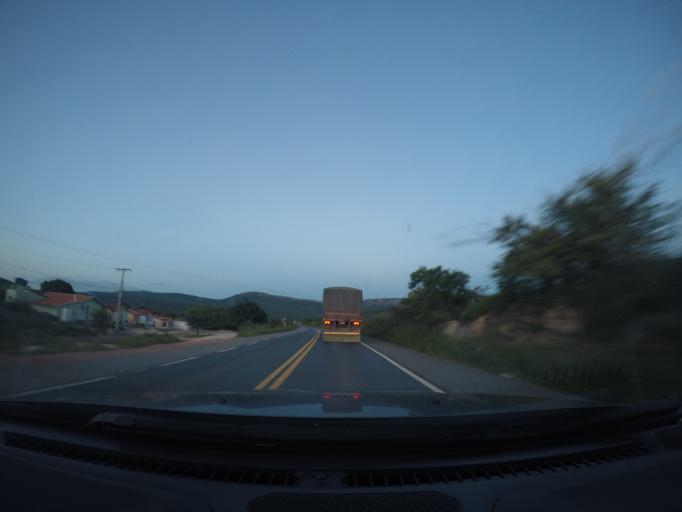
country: BR
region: Bahia
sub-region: Seabra
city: Seabra
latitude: -12.4836
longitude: -41.7214
